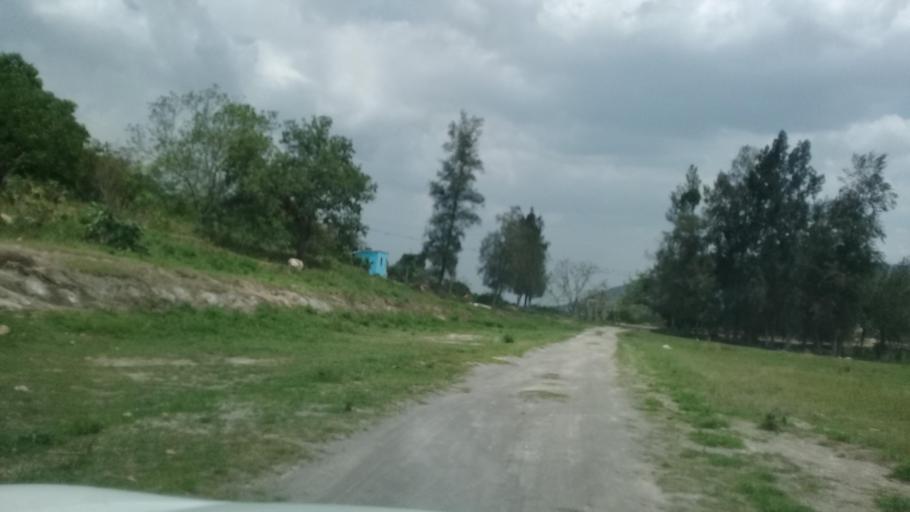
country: MX
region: Veracruz
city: Jalcomulco
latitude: 19.3840
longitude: -96.7936
